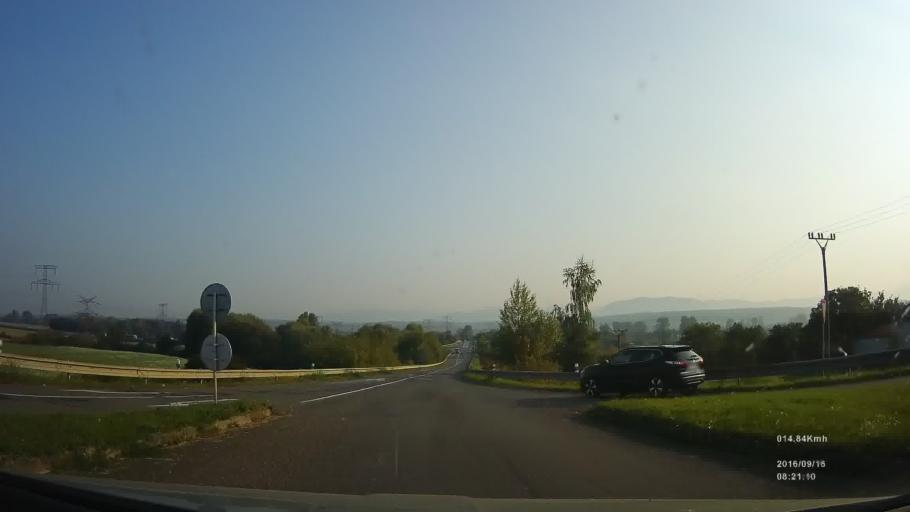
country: SK
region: Kosicky
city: Kosice
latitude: 48.8538
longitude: 21.2645
